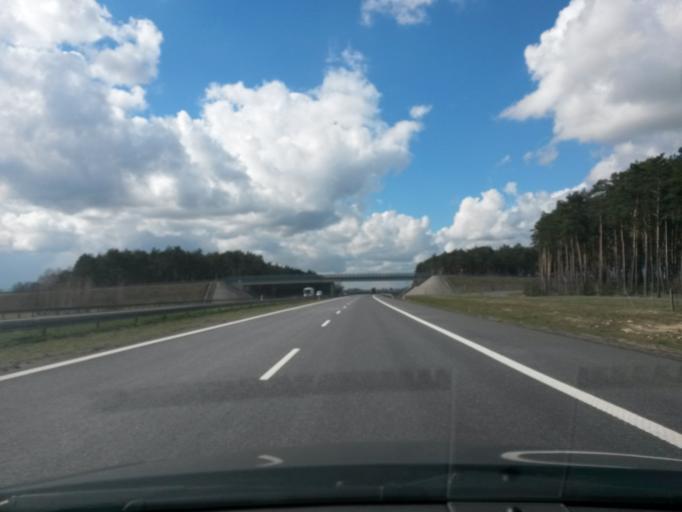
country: PL
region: Lodz Voivodeship
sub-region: Powiat leczycki
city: Swinice Warckie
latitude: 52.0318
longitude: 18.8896
